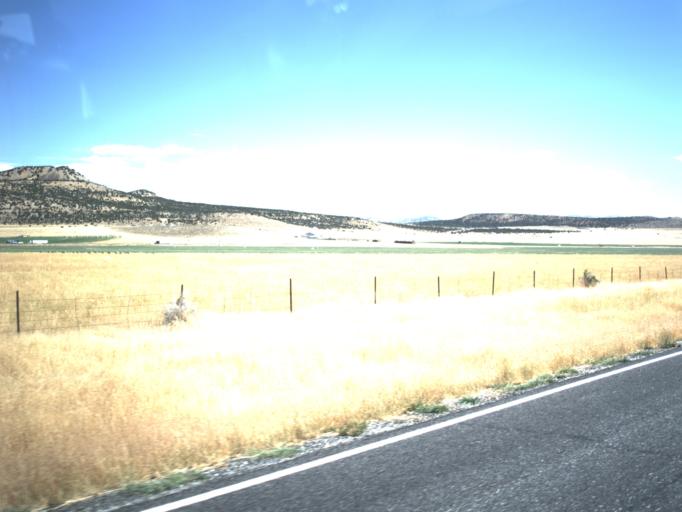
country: US
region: Idaho
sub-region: Oneida County
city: Malad City
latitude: 41.9669
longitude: -112.7930
